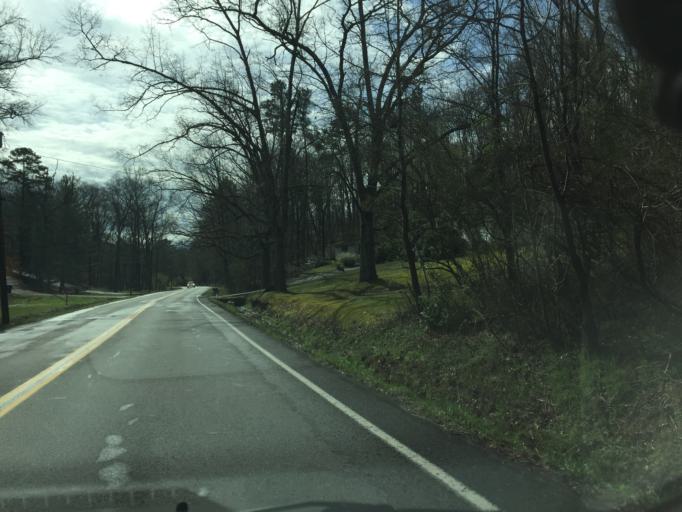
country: US
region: Tennessee
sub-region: Hamilton County
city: Collegedale
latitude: 35.0243
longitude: -85.0996
